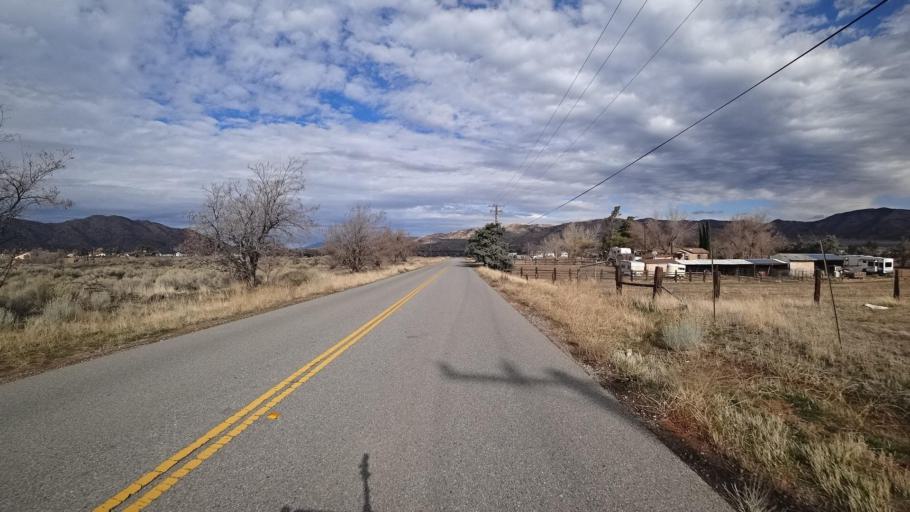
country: US
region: California
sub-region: Kern County
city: Golden Hills
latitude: 35.1256
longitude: -118.4776
